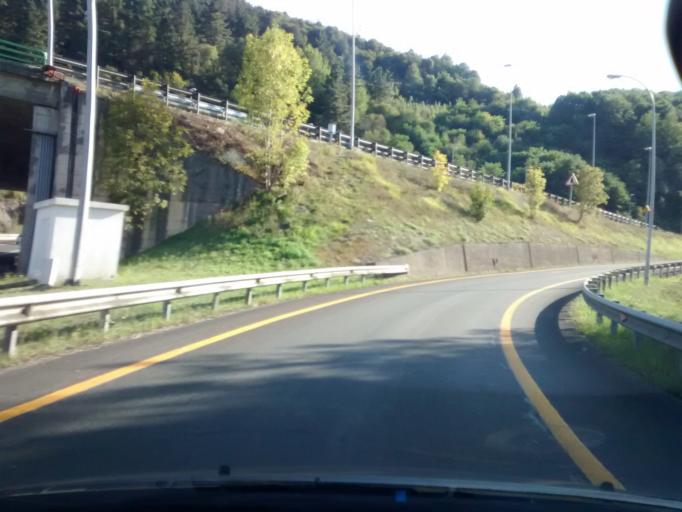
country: ES
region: Basque Country
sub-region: Bizkaia
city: Ermua
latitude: 43.1778
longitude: -2.4971
